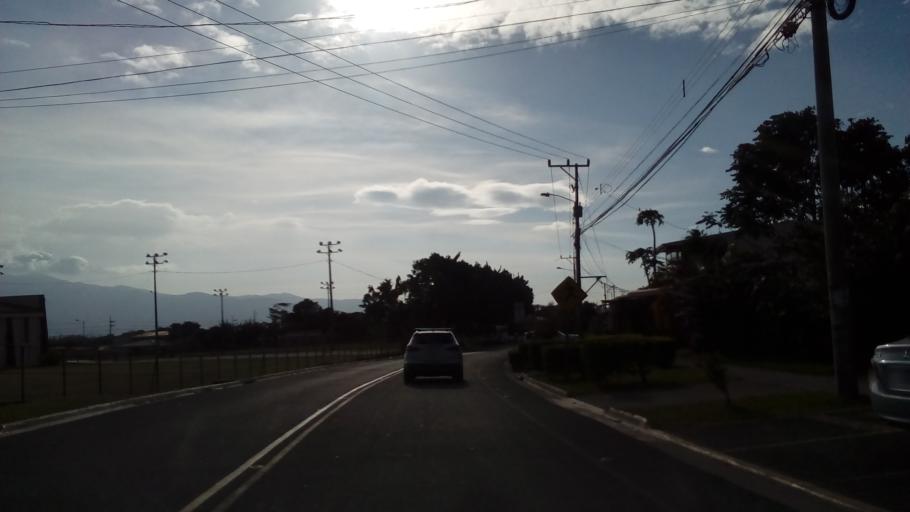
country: CR
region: Heredia
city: Angeles
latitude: 9.9891
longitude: -84.0594
